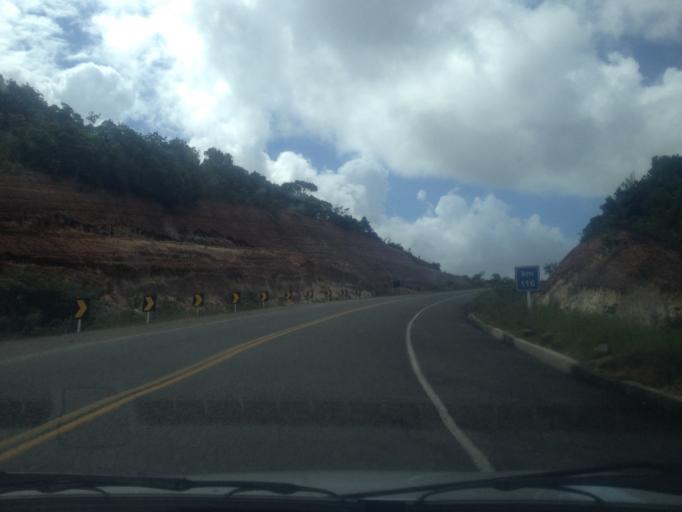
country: BR
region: Bahia
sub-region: Conde
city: Conde
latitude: -12.0851
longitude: -37.7720
